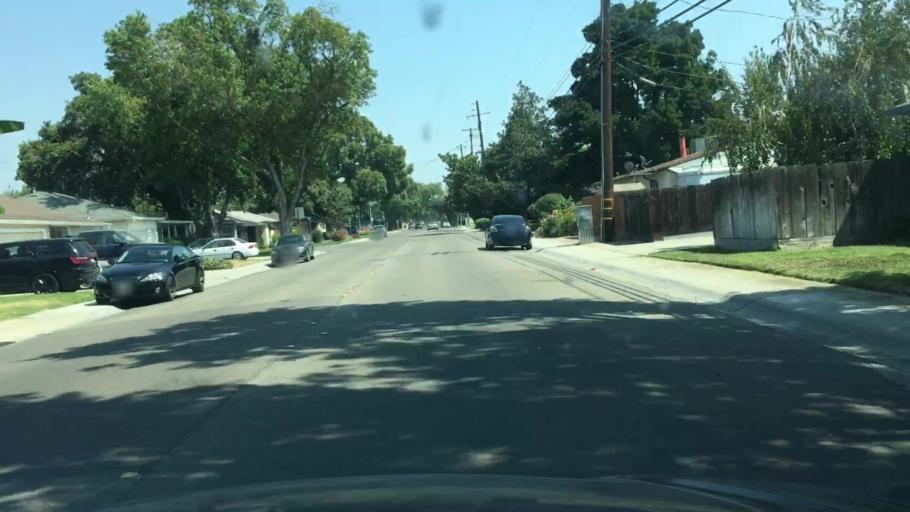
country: US
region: California
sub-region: San Joaquin County
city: Tracy
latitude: 37.7433
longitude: -121.4369
